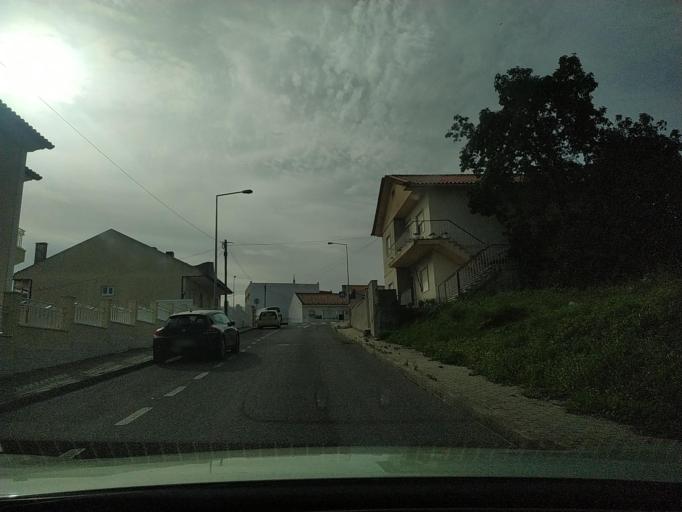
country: PT
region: Lisbon
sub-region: Amadora
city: Amadora
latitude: 38.7760
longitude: -9.2328
